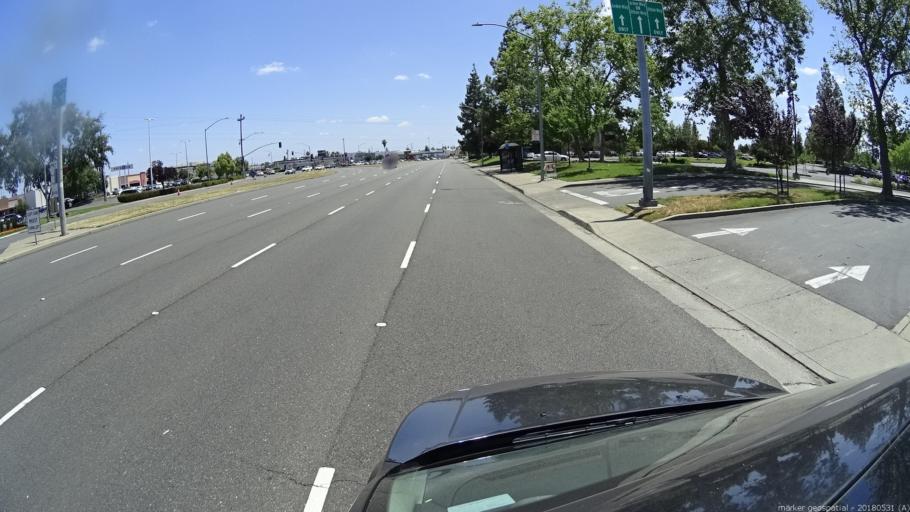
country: US
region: California
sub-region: Sacramento County
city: Arden-Arcade
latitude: 38.5974
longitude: -121.4229
